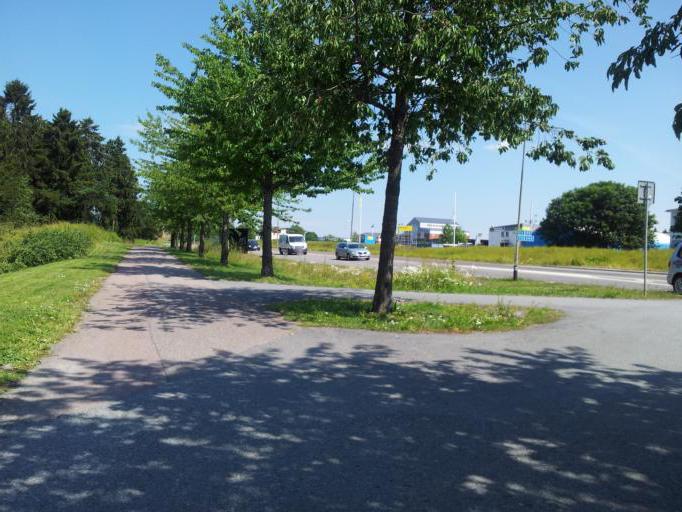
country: SE
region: Uppsala
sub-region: Uppsala Kommun
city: Saevja
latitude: 59.8491
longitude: 17.6805
